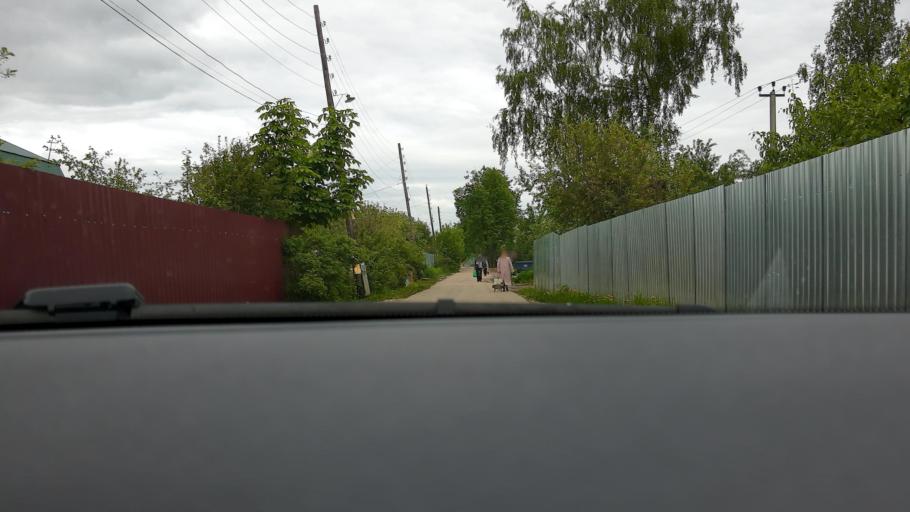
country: RU
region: Nizjnij Novgorod
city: Gorbatovka
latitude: 56.2595
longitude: 43.8327
